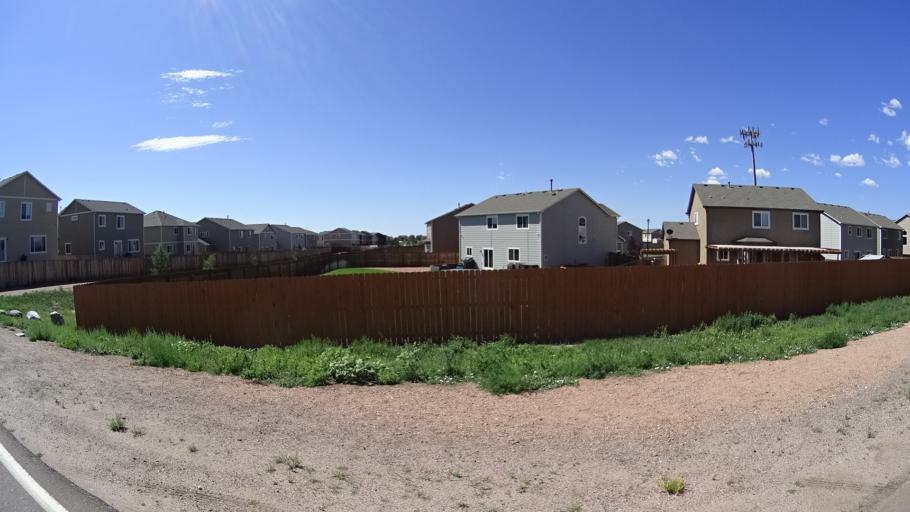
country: US
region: Colorado
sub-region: El Paso County
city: Security-Widefield
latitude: 38.7810
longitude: -104.6545
